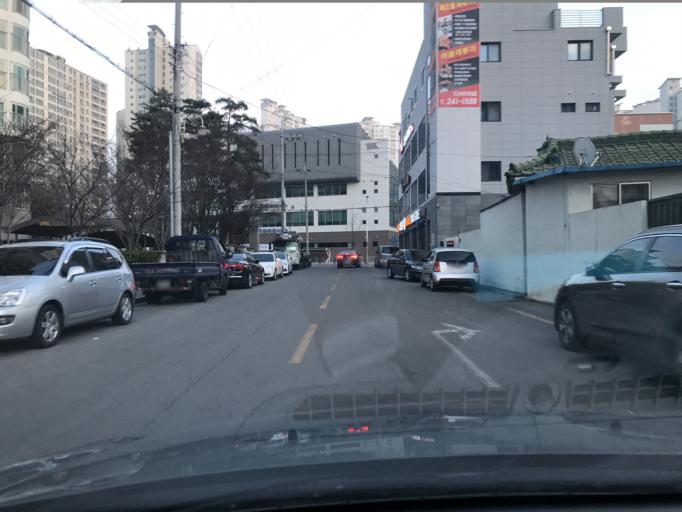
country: KR
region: Daegu
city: Hwawon
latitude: 35.8180
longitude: 128.5180
